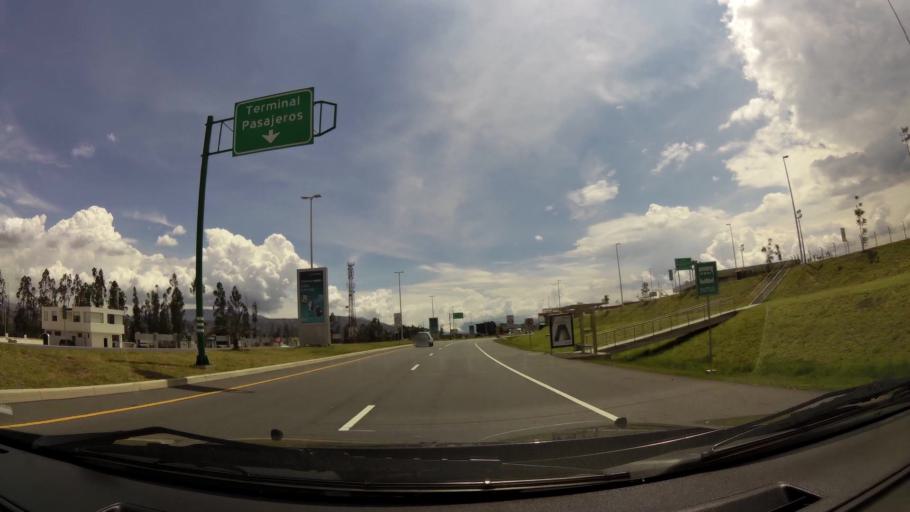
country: EC
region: Pichincha
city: Quito
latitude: -0.1382
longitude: -78.3579
